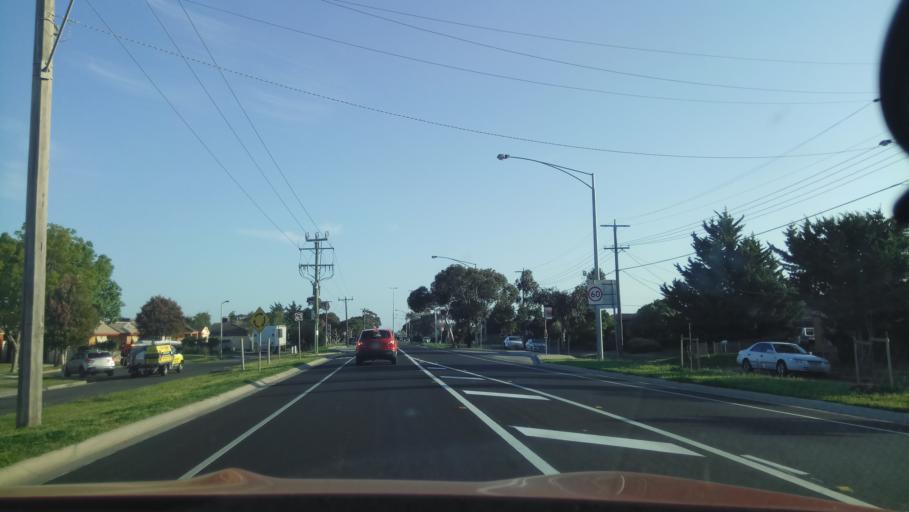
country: AU
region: Victoria
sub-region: Hobsons Bay
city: Laverton
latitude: -37.8811
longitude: 144.7571
